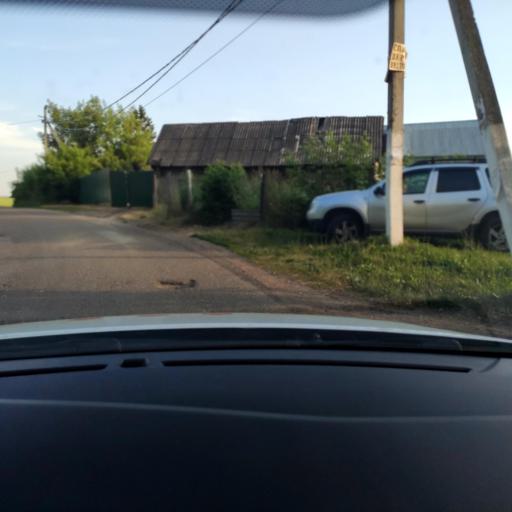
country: RU
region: Tatarstan
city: Vysokaya Gora
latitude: 55.9761
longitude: 49.3061
